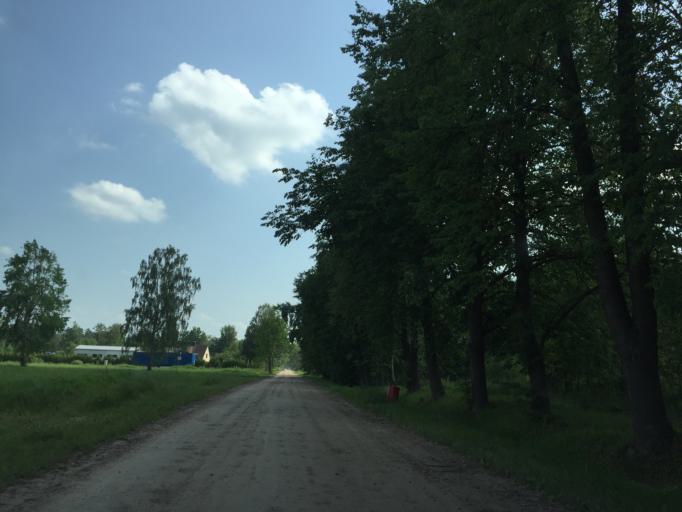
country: LV
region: Jelgava
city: Jelgava
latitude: 56.6792
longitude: 23.7396
